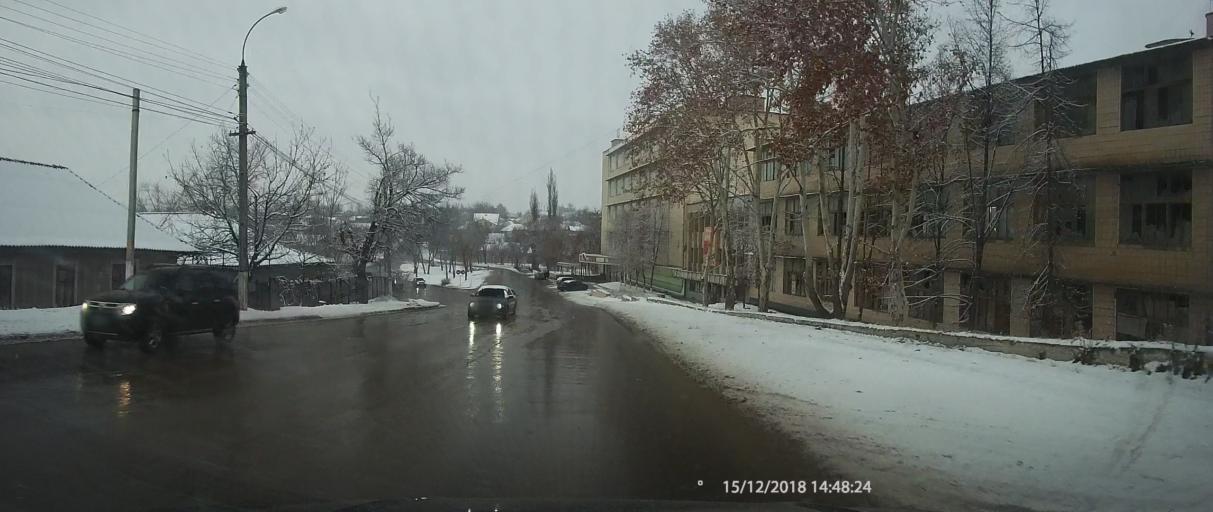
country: MD
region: Cahul
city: Cahul
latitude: 45.8971
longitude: 28.1981
